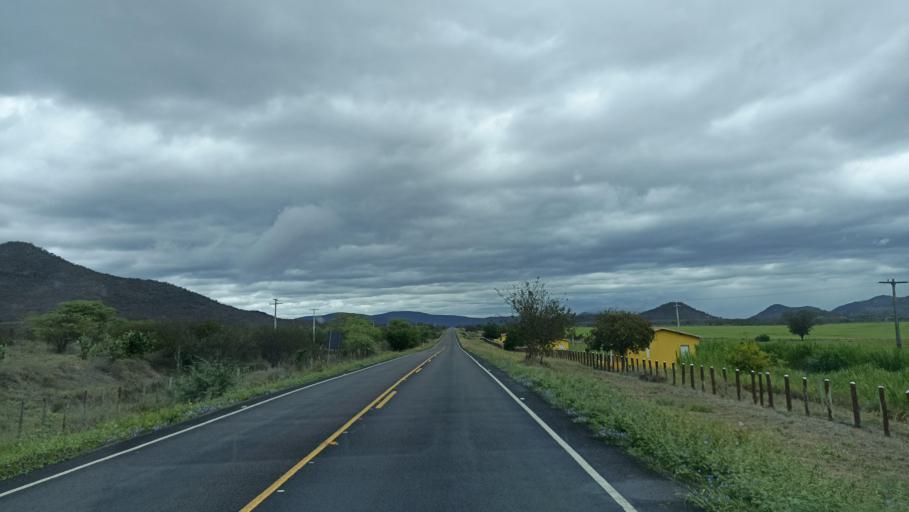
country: BR
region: Bahia
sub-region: Iacu
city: Iacu
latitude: -12.8915
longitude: -40.3968
